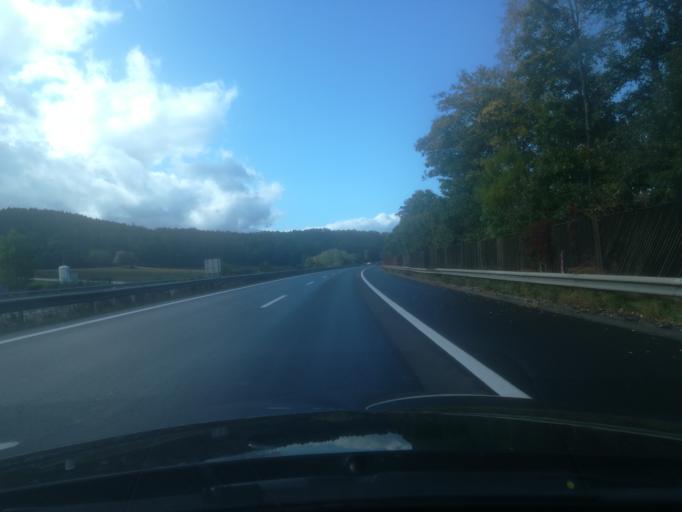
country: AT
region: Upper Austria
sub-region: Politischer Bezirk Urfahr-Umgebung
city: Engerwitzdorf
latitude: 48.3363
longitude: 14.4254
